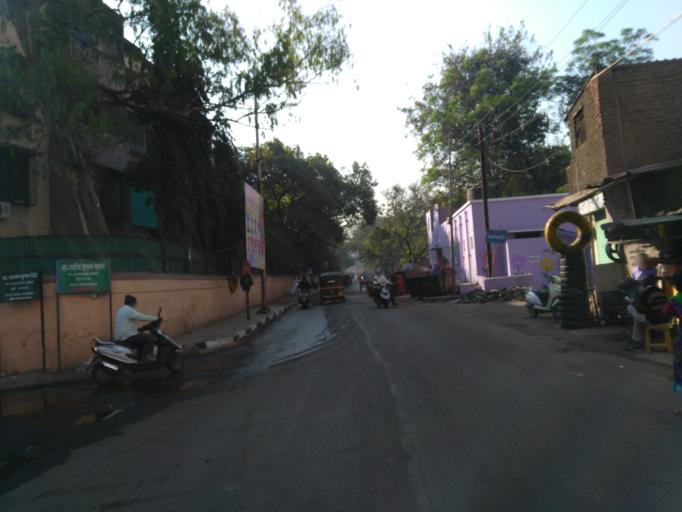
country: IN
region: Maharashtra
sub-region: Pune Division
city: Pune
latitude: 18.5138
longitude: 73.8713
